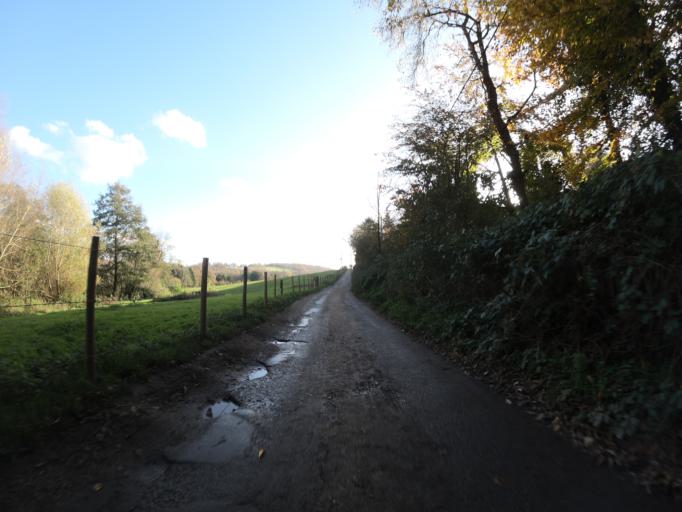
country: GB
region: England
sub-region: Kent
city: Eynsford
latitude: 51.3625
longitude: 0.1961
